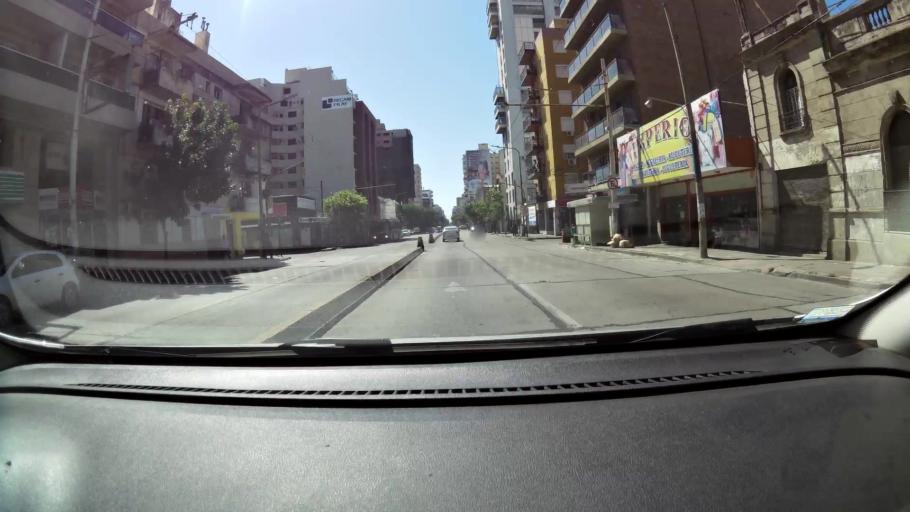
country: AR
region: Cordoba
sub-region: Departamento de Capital
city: Cordoba
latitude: -31.4073
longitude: -64.2049
